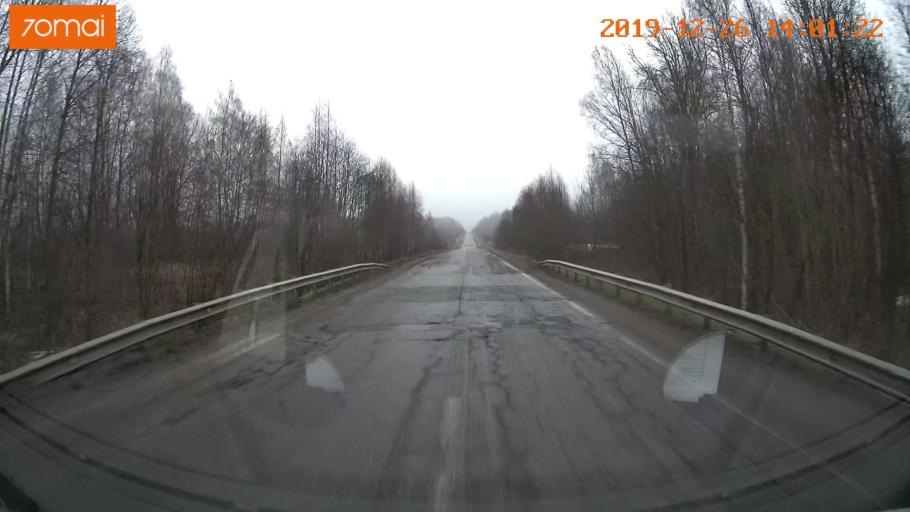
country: RU
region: Jaroslavl
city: Poshekhon'ye
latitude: 58.5509
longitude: 38.7628
